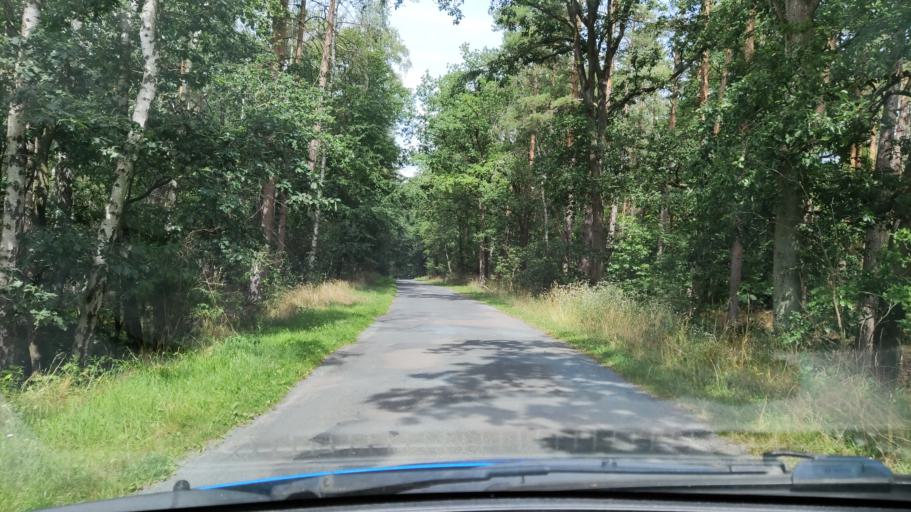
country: DE
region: Lower Saxony
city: Schnega
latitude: 52.9276
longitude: 10.9061
